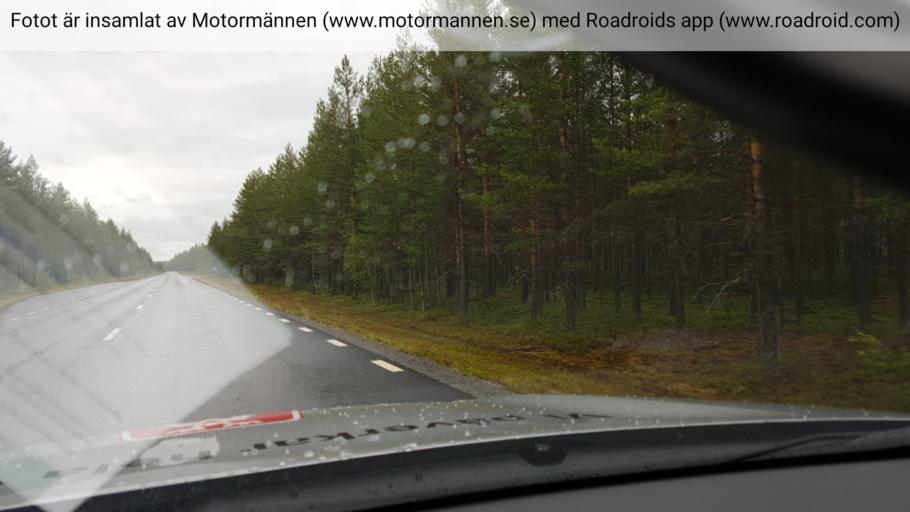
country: SE
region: Norrbotten
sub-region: Alvsbyns Kommun
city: AElvsbyn
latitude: 66.2454
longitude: 20.8603
